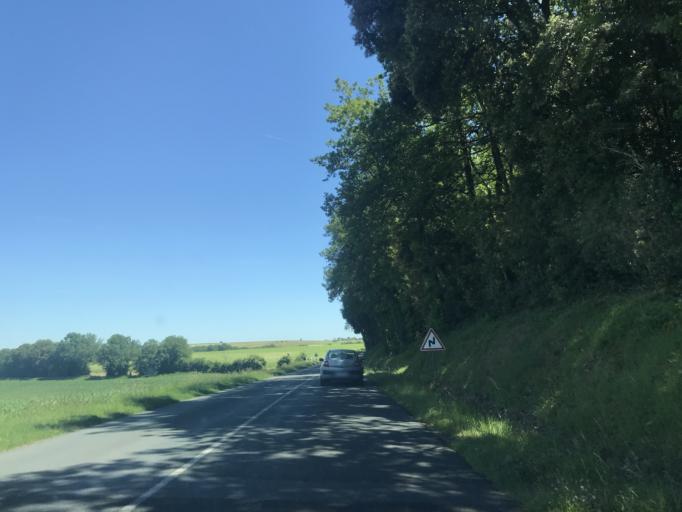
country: FR
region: Poitou-Charentes
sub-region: Departement de la Charente-Maritime
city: Meschers-sur-Gironde
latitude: 45.5928
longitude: -0.9680
